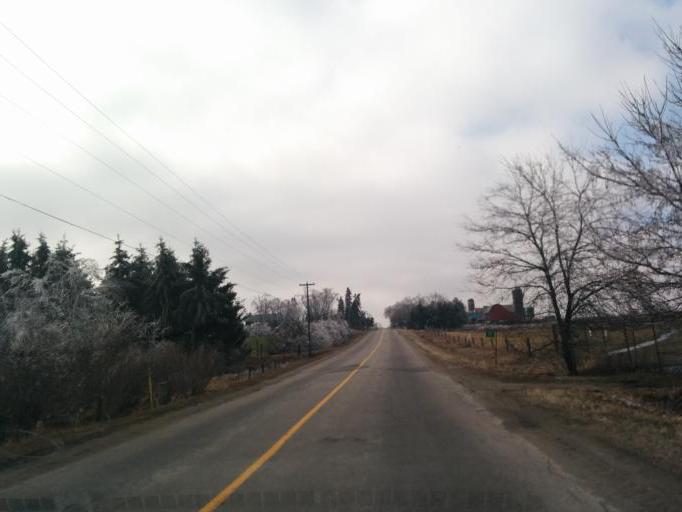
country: CA
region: Ontario
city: Waterloo
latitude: 43.6341
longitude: -80.5632
